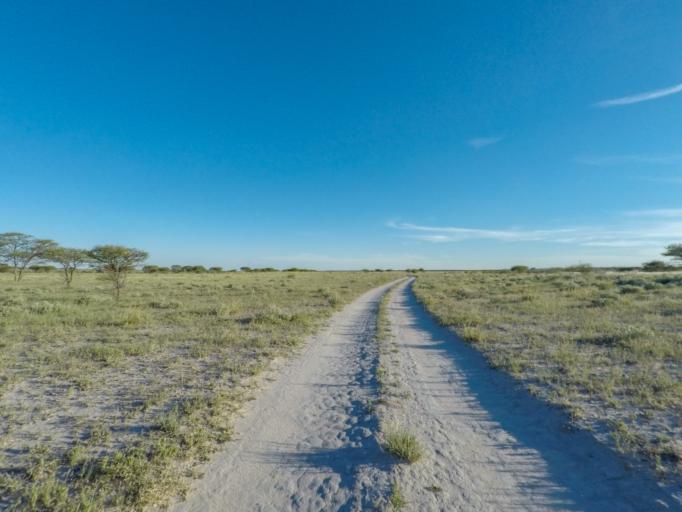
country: BW
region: Central
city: Rakops
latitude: -21.3857
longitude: 23.7950
